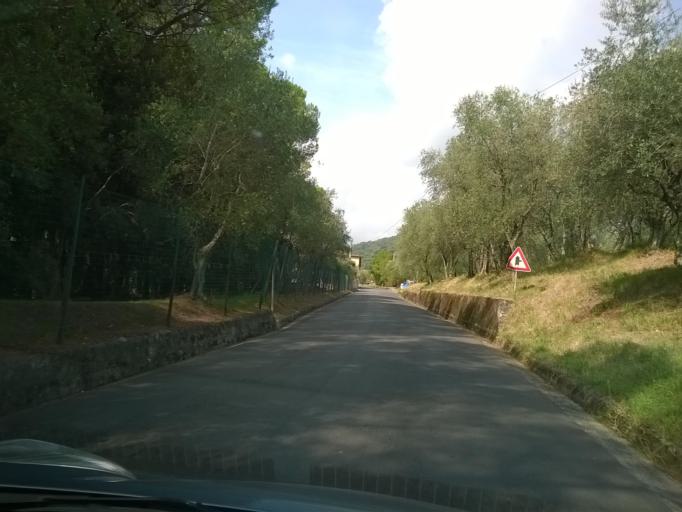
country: IT
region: Tuscany
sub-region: Provincia di Pistoia
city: Pescia
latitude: 43.8944
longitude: 10.6807
